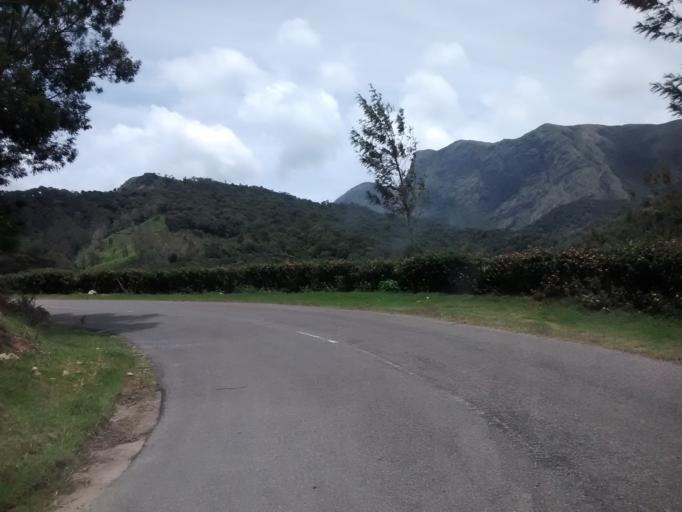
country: IN
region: Kerala
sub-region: Idukki
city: Munnar
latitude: 10.1269
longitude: 77.2172
